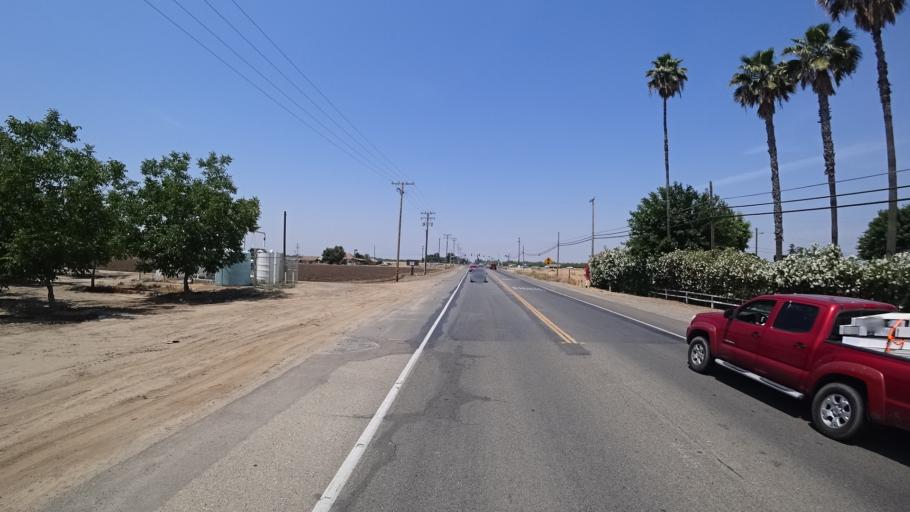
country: US
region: California
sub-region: Kings County
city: Armona
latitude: 36.3280
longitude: -119.6884
